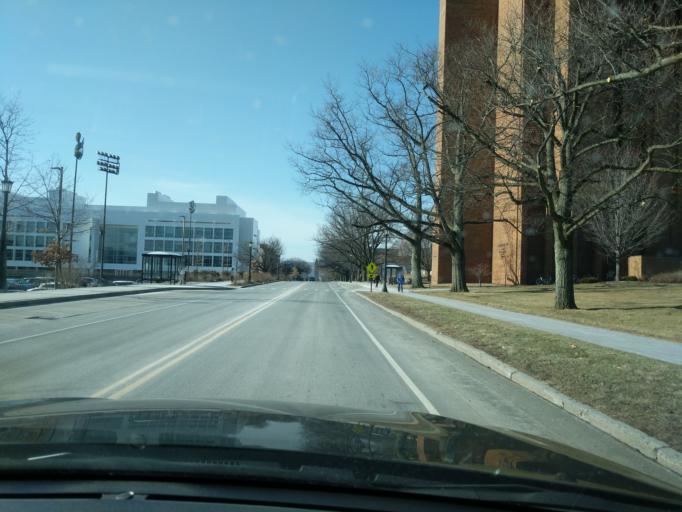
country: US
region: New York
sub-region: Tompkins County
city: East Ithaca
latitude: 42.4476
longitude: -76.4749
